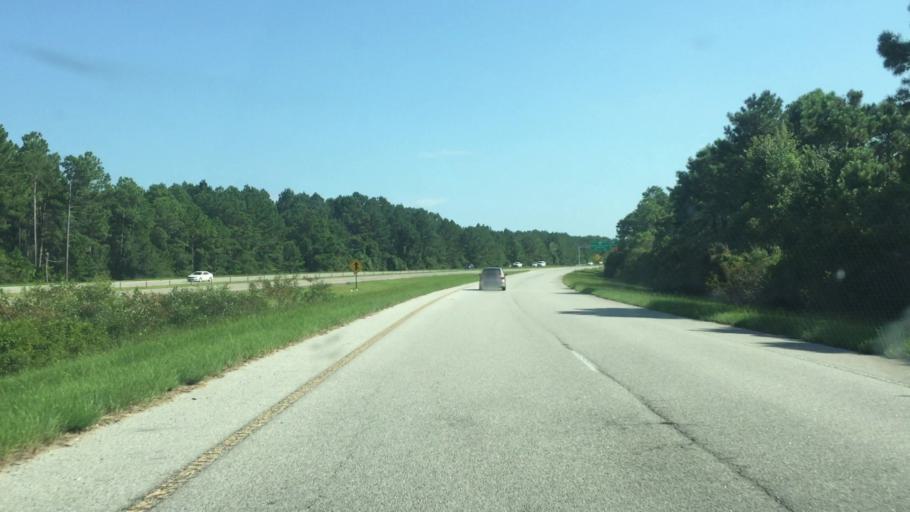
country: US
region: South Carolina
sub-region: Horry County
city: North Myrtle Beach
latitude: 33.8057
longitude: -78.7794
